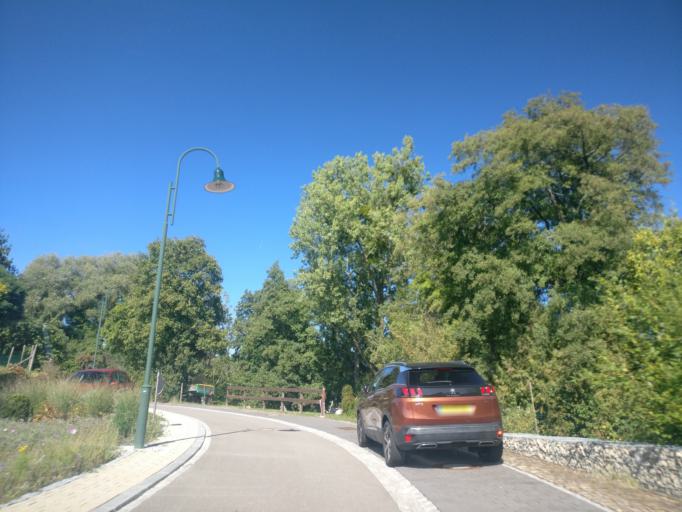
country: LU
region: Grevenmacher
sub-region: Canton de Grevenmacher
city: Wormeldange
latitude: 49.6362
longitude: 6.4098
